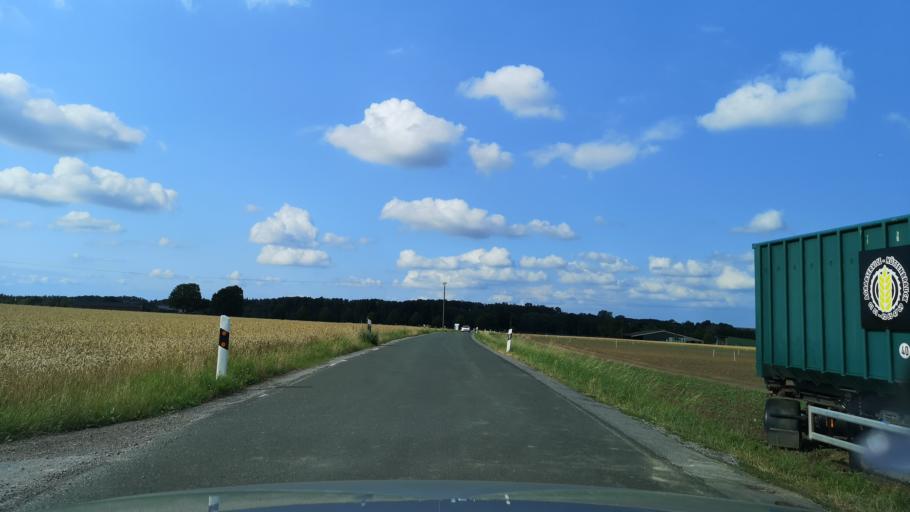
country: DE
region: North Rhine-Westphalia
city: Iserlohn
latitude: 51.4329
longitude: 7.7093
